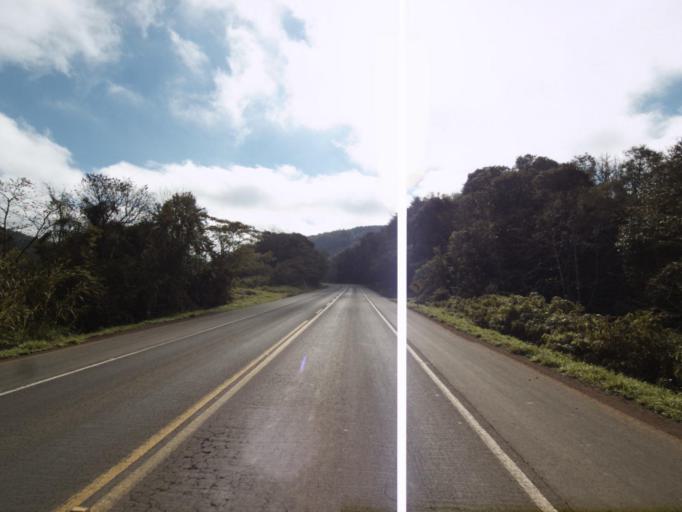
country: BR
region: Rio Grande do Sul
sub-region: Frederico Westphalen
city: Frederico Westphalen
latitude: -27.1474
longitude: -53.2133
